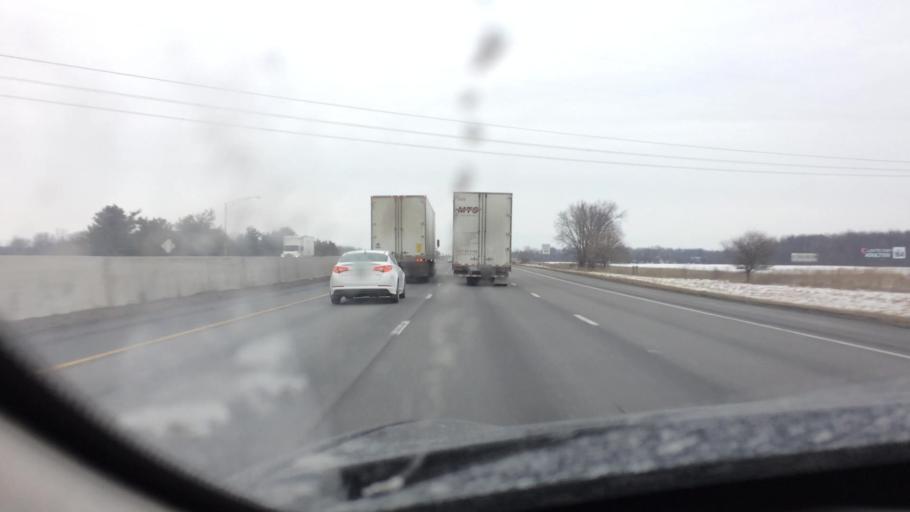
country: US
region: Ohio
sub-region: Hancock County
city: Findlay
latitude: 41.0967
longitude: -83.6597
